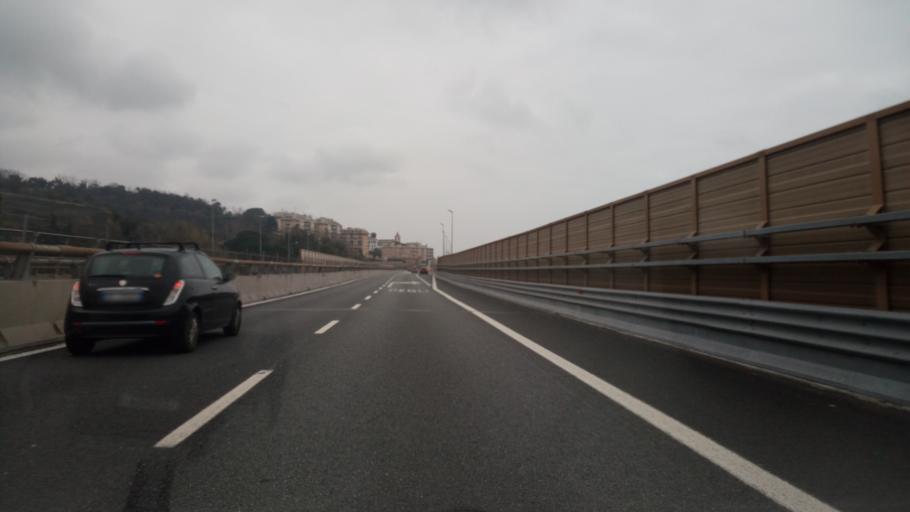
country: IT
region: Liguria
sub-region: Provincia di Genova
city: Mele
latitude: 44.4302
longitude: 8.8198
